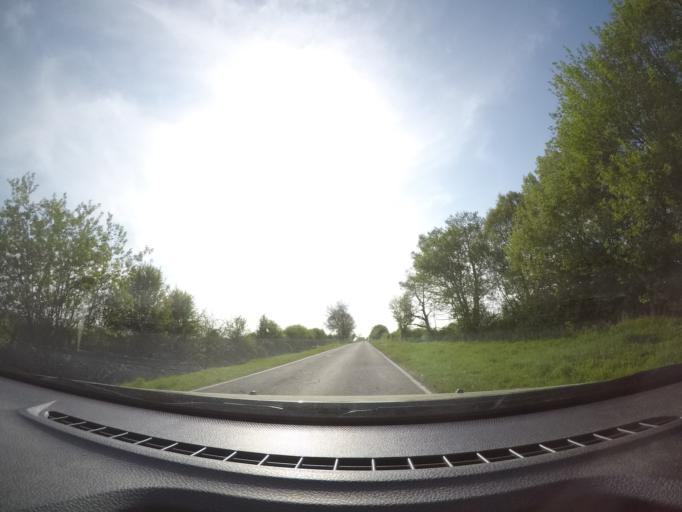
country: BE
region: Wallonia
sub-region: Province du Luxembourg
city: Tintigny
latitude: 49.6641
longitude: 5.5060
